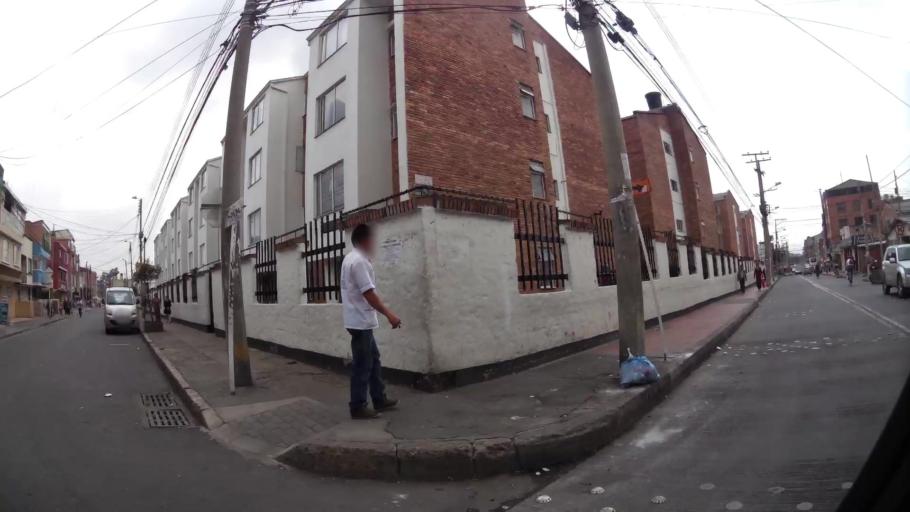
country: CO
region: Cundinamarca
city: La Calera
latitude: 4.7326
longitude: -74.0271
